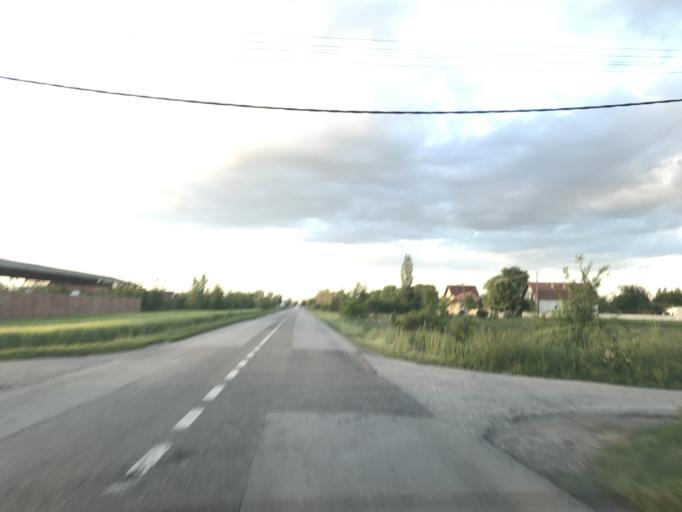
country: RS
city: Banatsko Karadordevo
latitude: 45.5871
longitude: 20.5534
